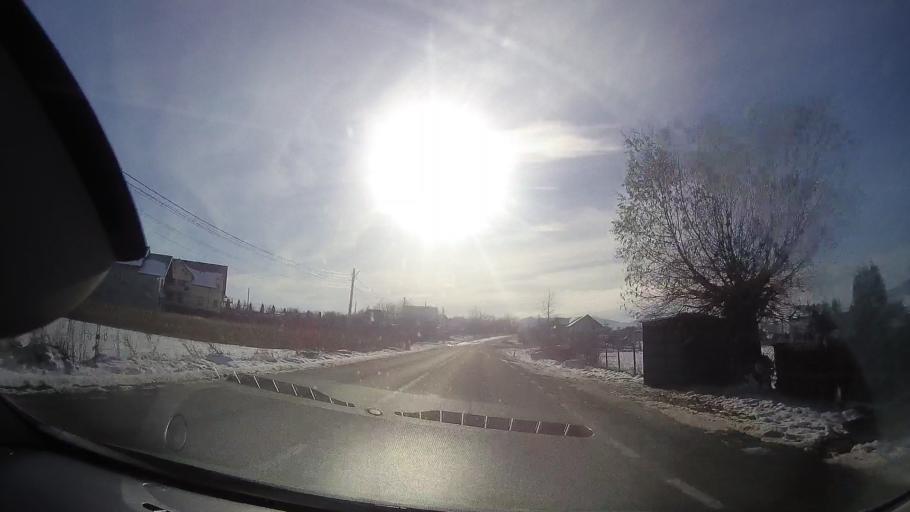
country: RO
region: Neamt
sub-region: Comuna Baltatesti
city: Valea Seaca
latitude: 47.1407
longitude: 26.3178
